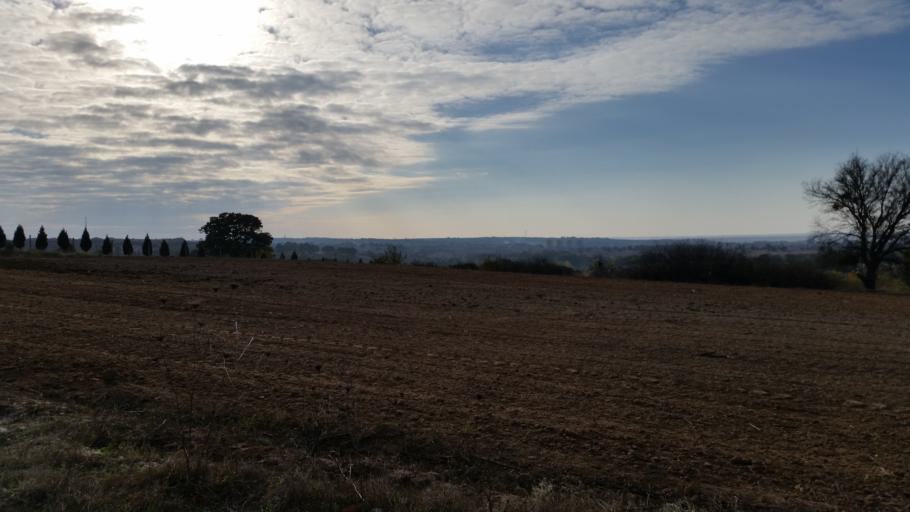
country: TR
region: Tekirdag
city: Cerkezkoey
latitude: 41.3702
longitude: 27.9711
